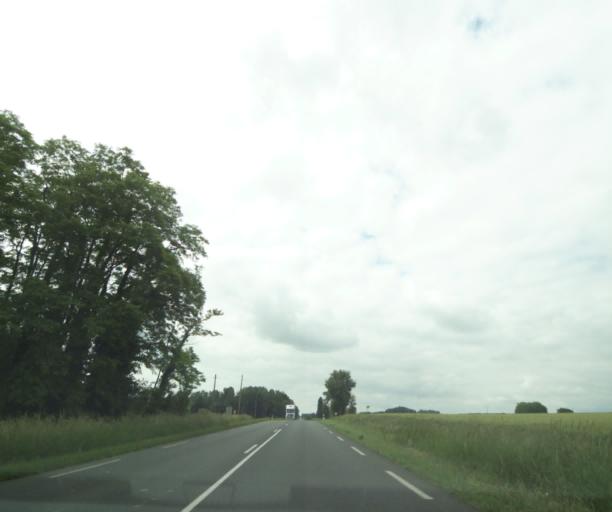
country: FR
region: Pays de la Loire
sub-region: Departement de Maine-et-Loire
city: Distre
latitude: 47.1895
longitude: -0.1287
